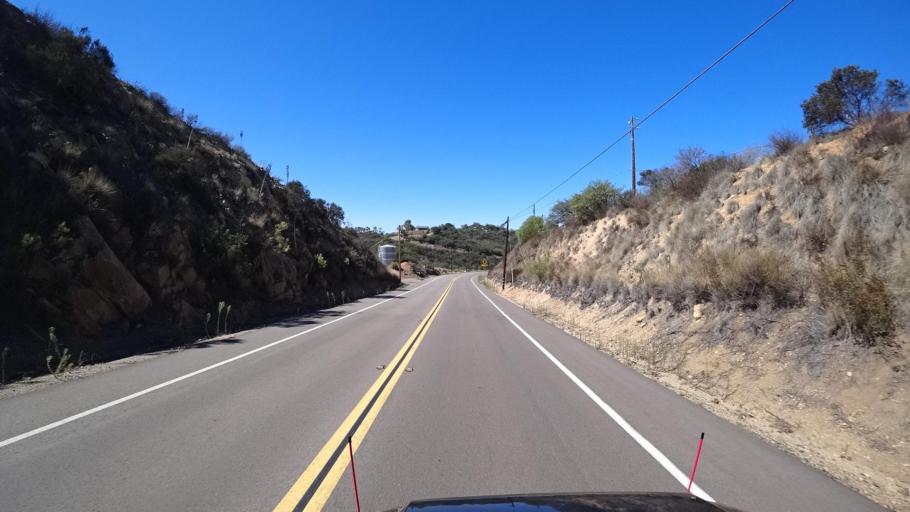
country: US
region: California
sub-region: San Diego County
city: Jamul
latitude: 32.7331
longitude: -116.8179
